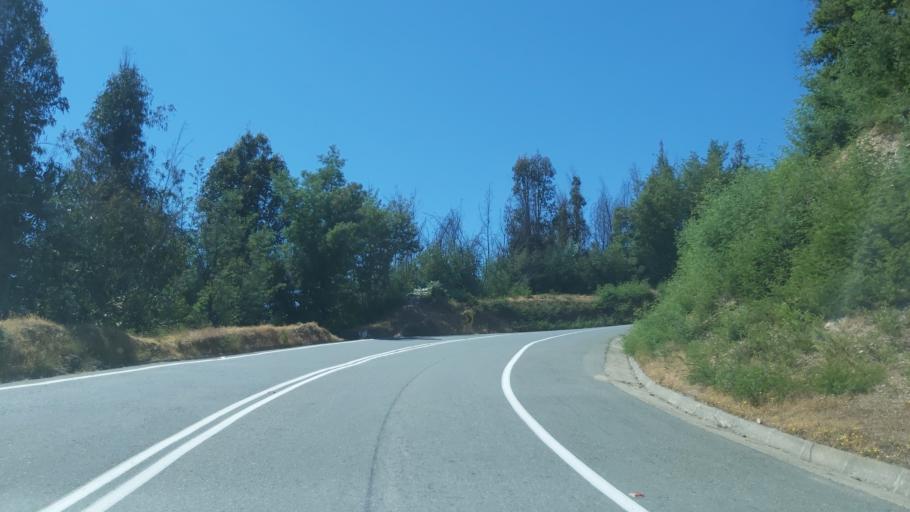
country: CL
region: Maule
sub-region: Provincia de Talca
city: Constitucion
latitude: -34.9101
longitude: -71.9965
